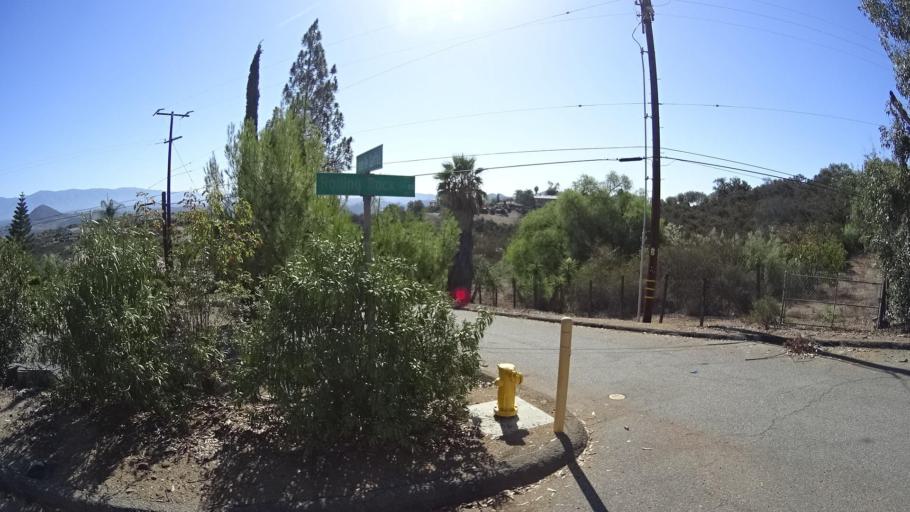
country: US
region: California
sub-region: San Diego County
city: Hidden Meadows
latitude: 33.2298
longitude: -117.1103
